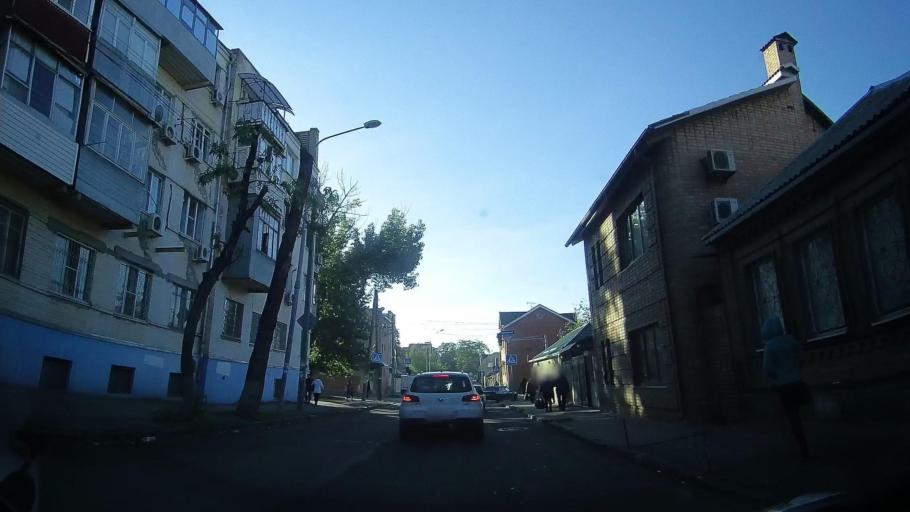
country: RU
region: Rostov
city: Rostov-na-Donu
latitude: 47.2332
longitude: 39.6960
